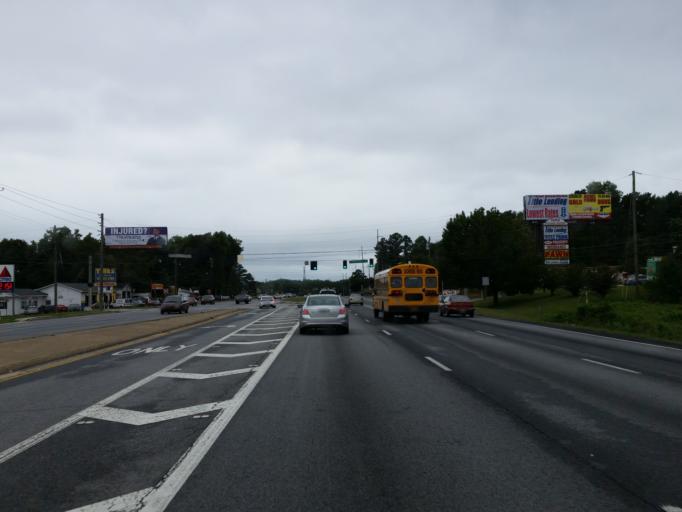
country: US
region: Georgia
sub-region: Clayton County
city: Jonesboro
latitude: 33.5523
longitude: -84.3703
